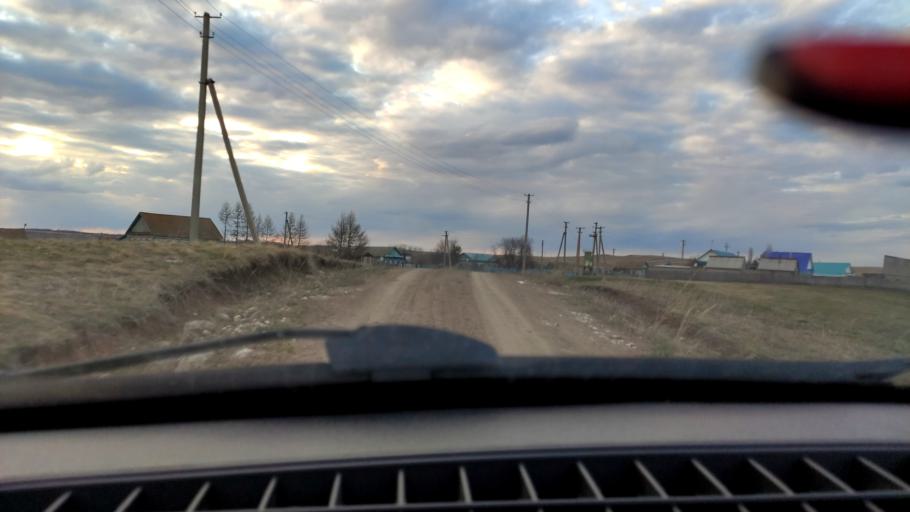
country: RU
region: Bashkortostan
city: Tolbazy
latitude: 54.0166
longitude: 55.5332
